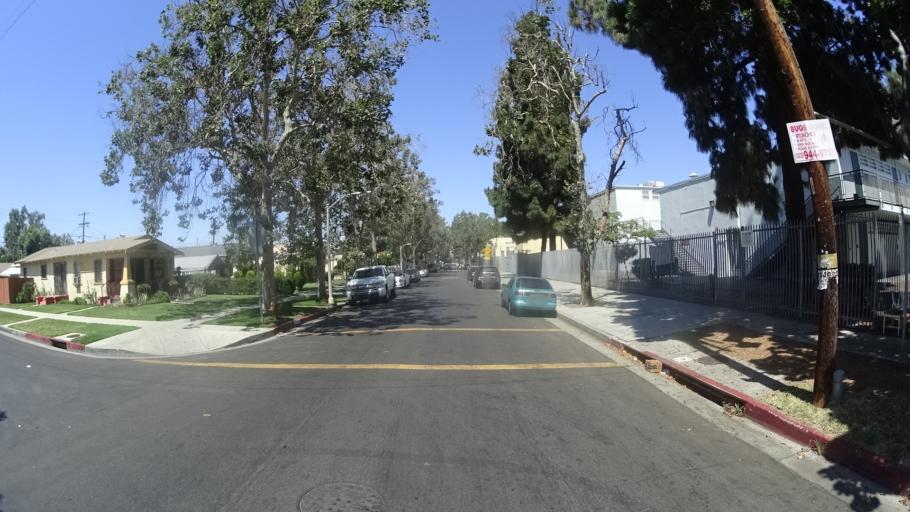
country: US
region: California
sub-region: Los Angeles County
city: Westmont
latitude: 33.9859
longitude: -118.2936
